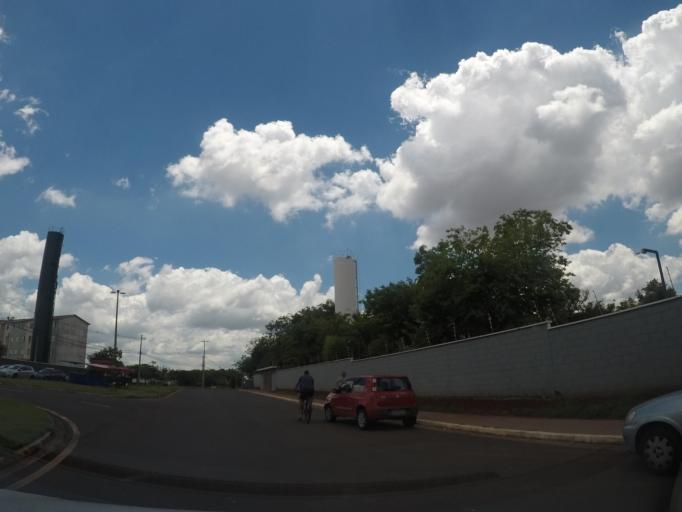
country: BR
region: Sao Paulo
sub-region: Hortolandia
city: Hortolandia
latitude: -22.8298
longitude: -47.2200
